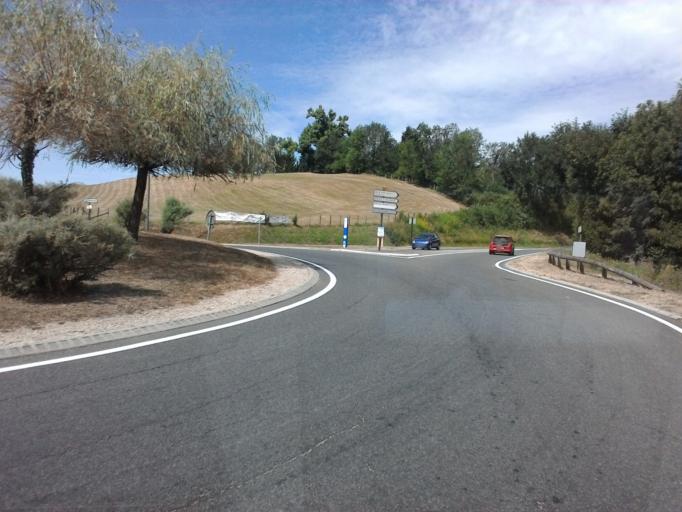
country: FR
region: Rhone-Alpes
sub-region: Departement de l'Isere
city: Le Pin
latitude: 45.4491
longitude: 5.5128
